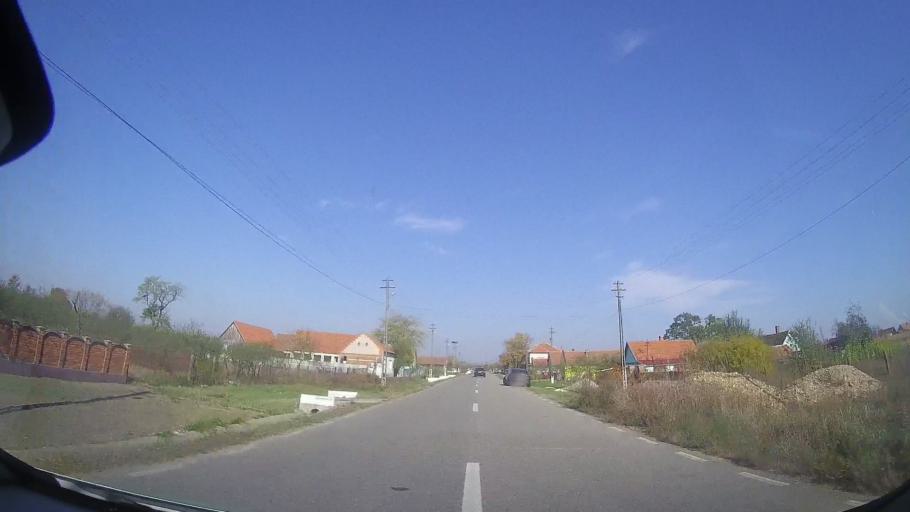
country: RO
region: Timis
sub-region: Comuna Ghizela
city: Ghizela
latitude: 45.7927
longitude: 21.7290
